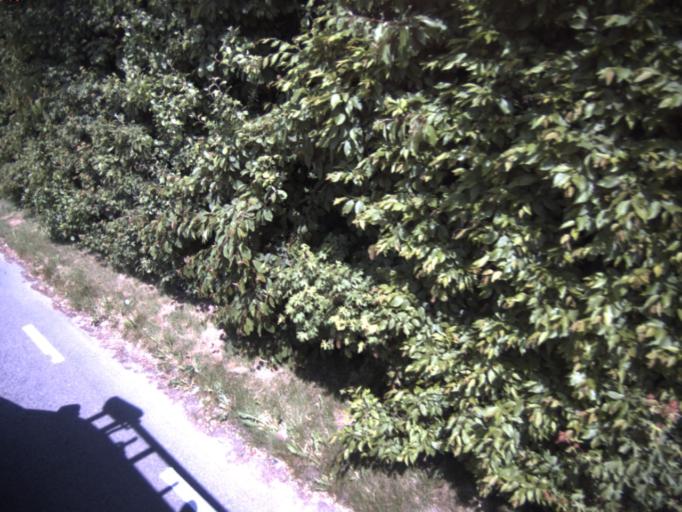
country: SE
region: Skane
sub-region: Helsingborg
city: Helsingborg
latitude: 56.0960
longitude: 12.6545
